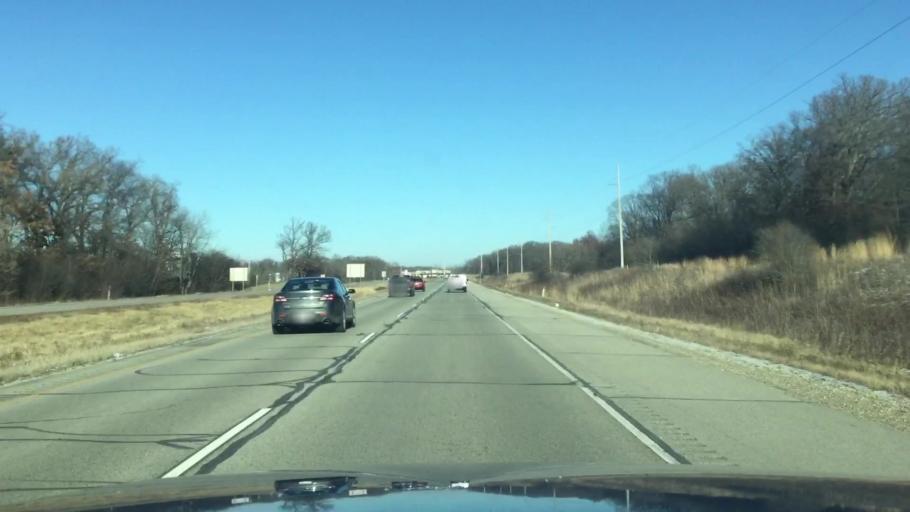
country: US
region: Wisconsin
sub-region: Racine County
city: Waterford
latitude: 42.7559
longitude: -88.2052
